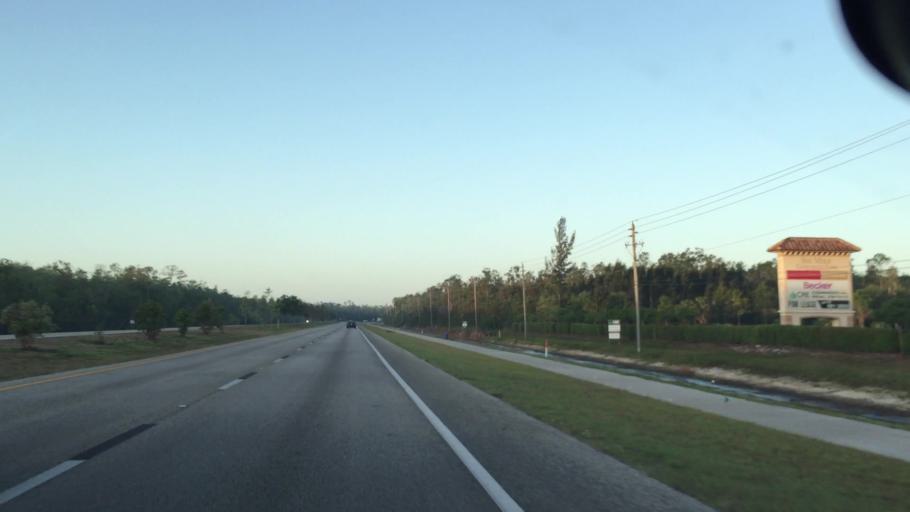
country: US
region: Florida
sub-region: Lee County
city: Villas
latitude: 26.5645
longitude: -81.8305
